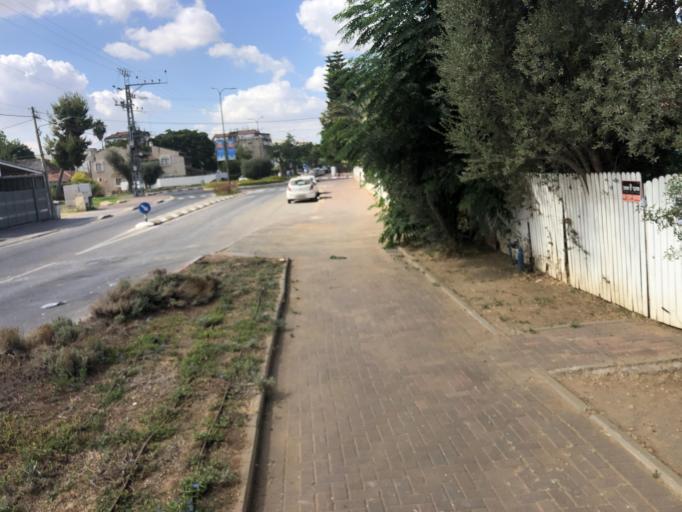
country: IL
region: Central District
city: Yehud
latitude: 32.0351
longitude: 34.8977
